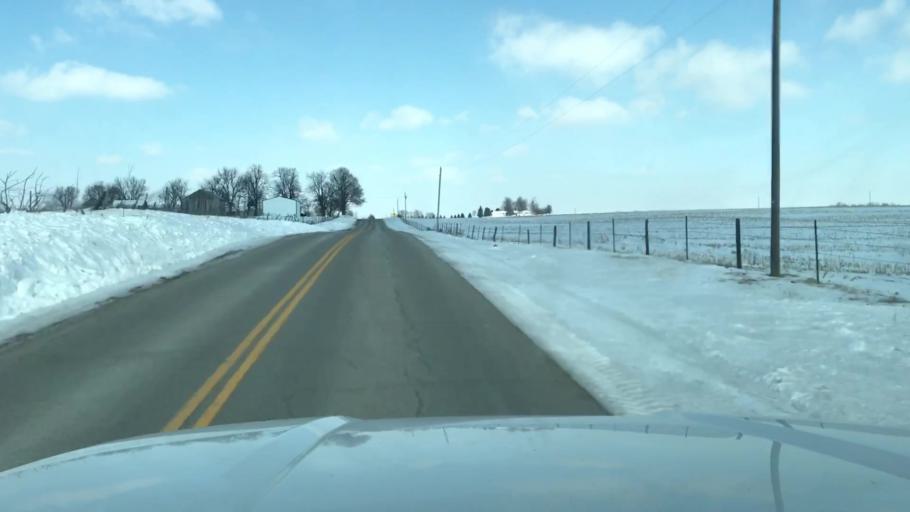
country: US
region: Missouri
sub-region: Nodaway County
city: Maryville
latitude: 40.3545
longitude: -94.7221
